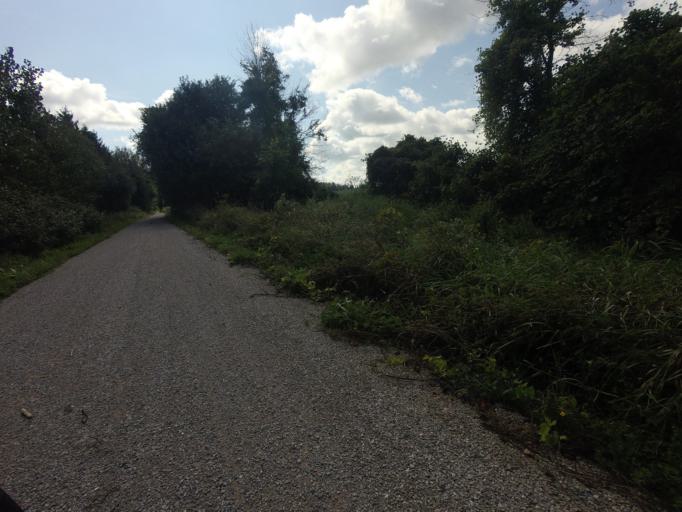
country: CA
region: Ontario
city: Huron East
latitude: 43.7008
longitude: -81.3495
